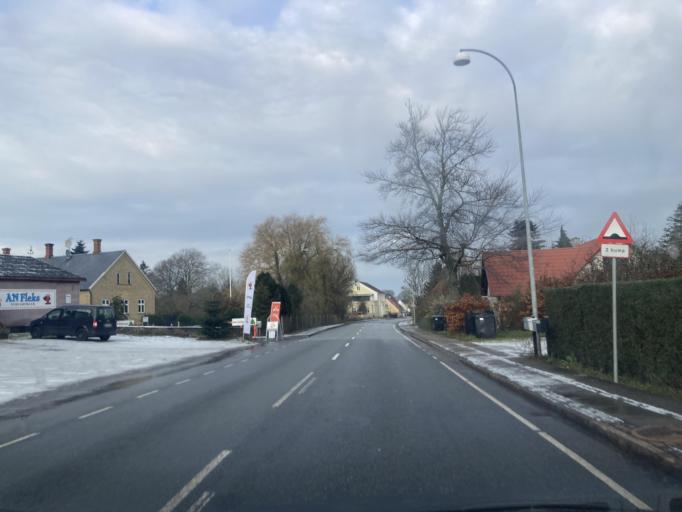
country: DK
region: Zealand
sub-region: Holbaek Kommune
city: Jyderup
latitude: 55.7085
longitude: 11.3845
